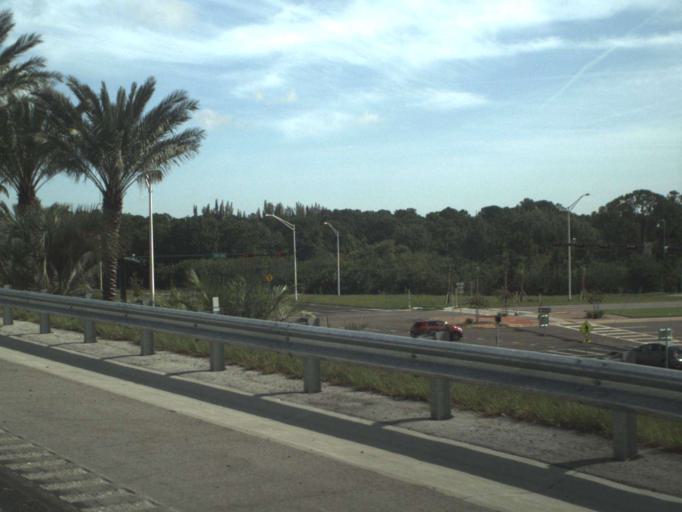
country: US
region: Florida
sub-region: Indian River County
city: West Vero Corridor
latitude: 27.6386
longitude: -80.5175
